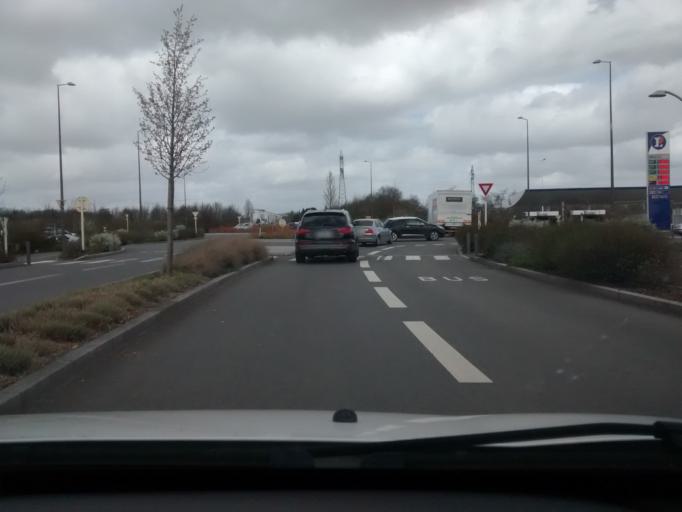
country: FR
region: Brittany
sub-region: Departement d'Ille-et-Vilaine
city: Saint-Gregoire
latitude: 48.1394
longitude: -1.6865
